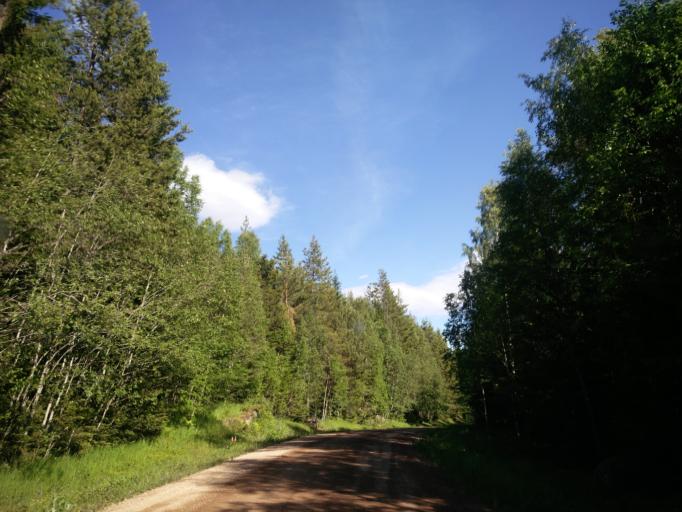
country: SE
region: Vaesternorrland
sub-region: Ange Kommun
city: Fransta
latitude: 62.2101
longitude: 16.3223
